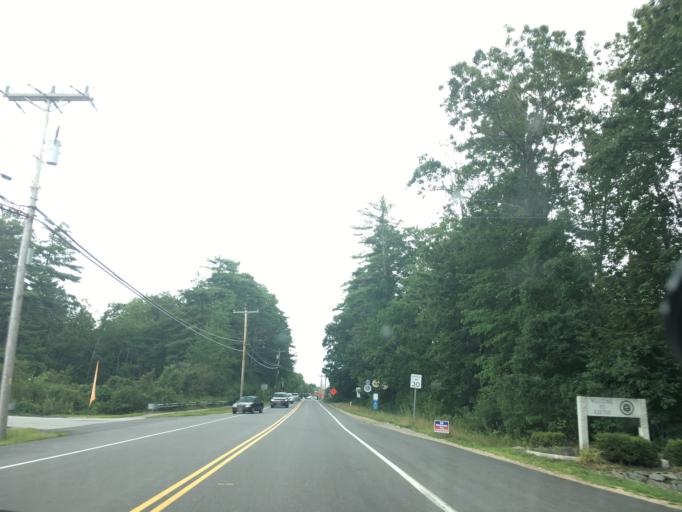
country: US
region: New Hampshire
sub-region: Rockingham County
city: Exeter
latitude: 42.9988
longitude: -70.9742
